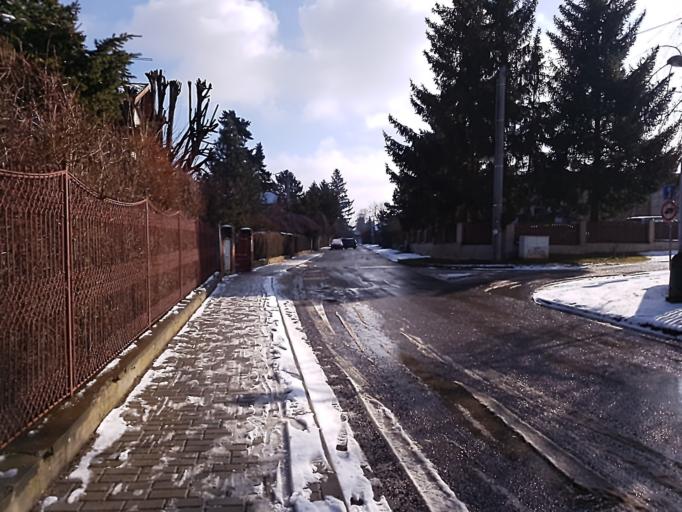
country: CZ
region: Central Bohemia
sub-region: Okres Praha-Vychod
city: Ricany
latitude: 49.9990
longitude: 14.6738
